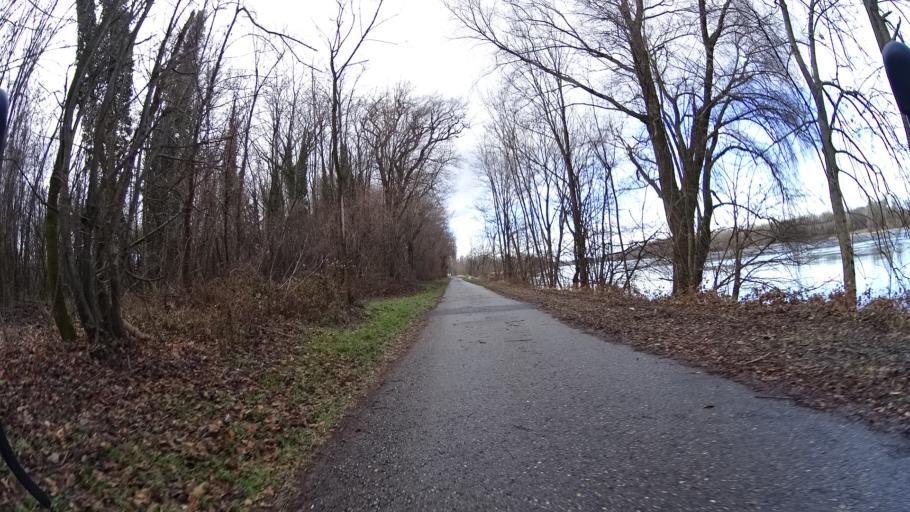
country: AT
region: Lower Austria
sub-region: Politischer Bezirk Tulln
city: Atzenbrugg
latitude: 48.3468
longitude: 15.9158
